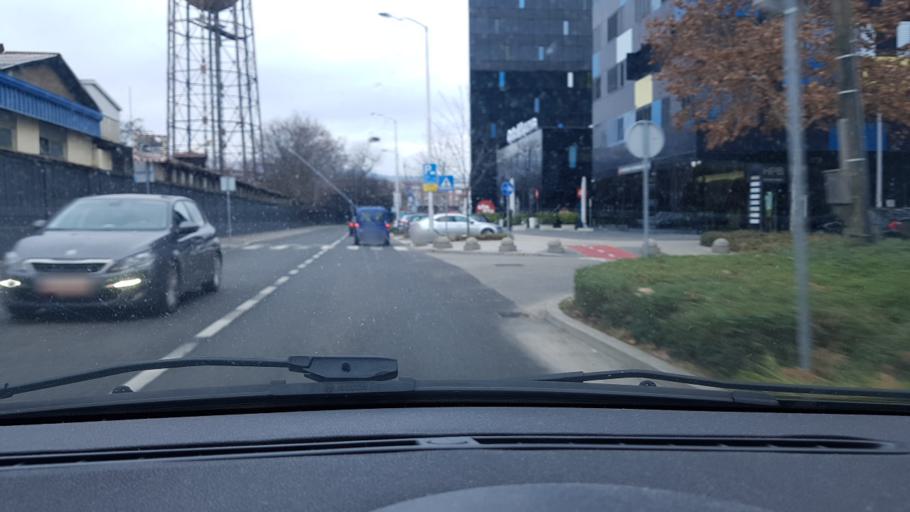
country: HR
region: Grad Zagreb
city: Zagreb - Centar
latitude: 45.8025
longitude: 15.9891
